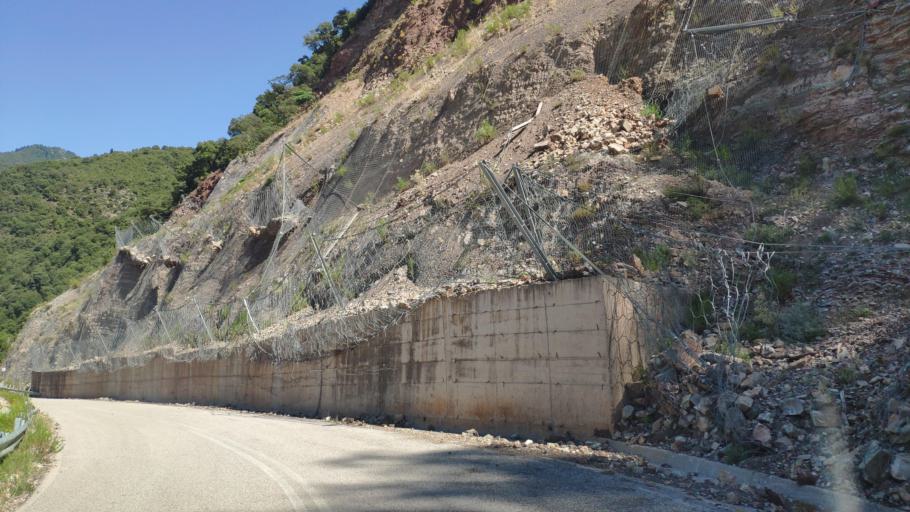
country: GR
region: Central Greece
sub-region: Nomos Evrytanias
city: Kerasochori
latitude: 39.0342
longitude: 21.5990
